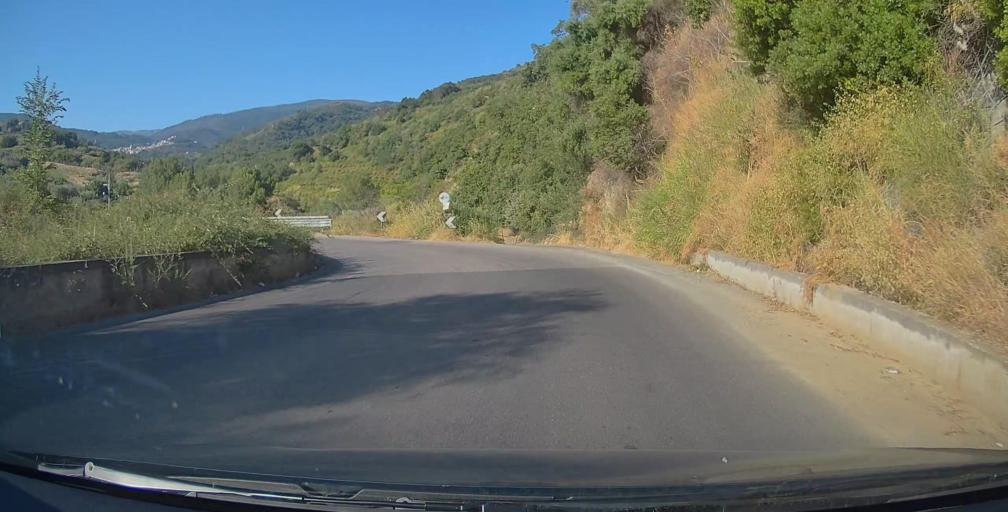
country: IT
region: Sicily
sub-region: Messina
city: Librizzi
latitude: 38.0776
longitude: 14.9720
